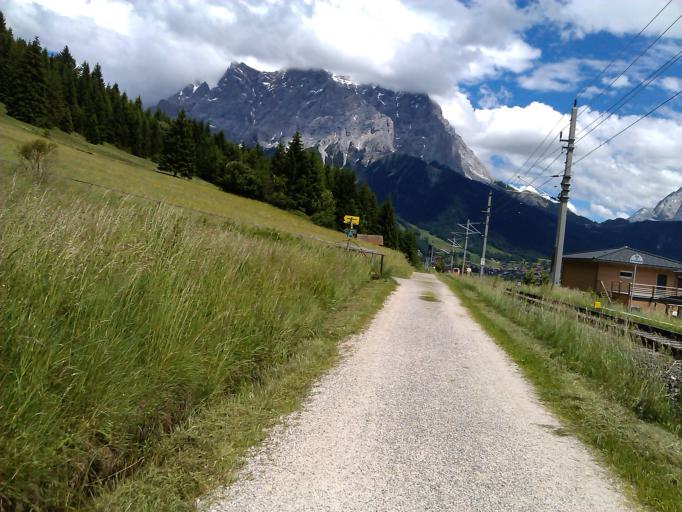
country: AT
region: Tyrol
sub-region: Politischer Bezirk Reutte
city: Lermoos
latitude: 47.4053
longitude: 10.8814
